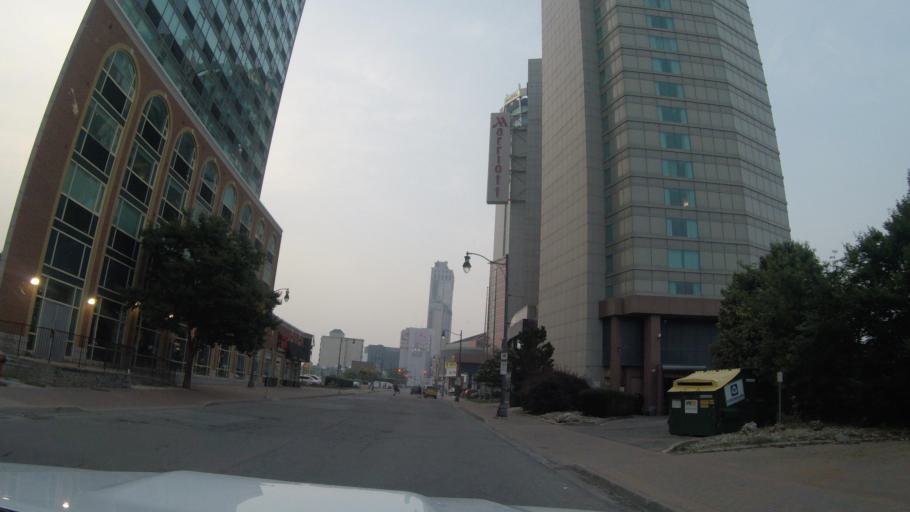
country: CA
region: Ontario
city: Niagara Falls
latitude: 43.0776
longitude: -79.0823
